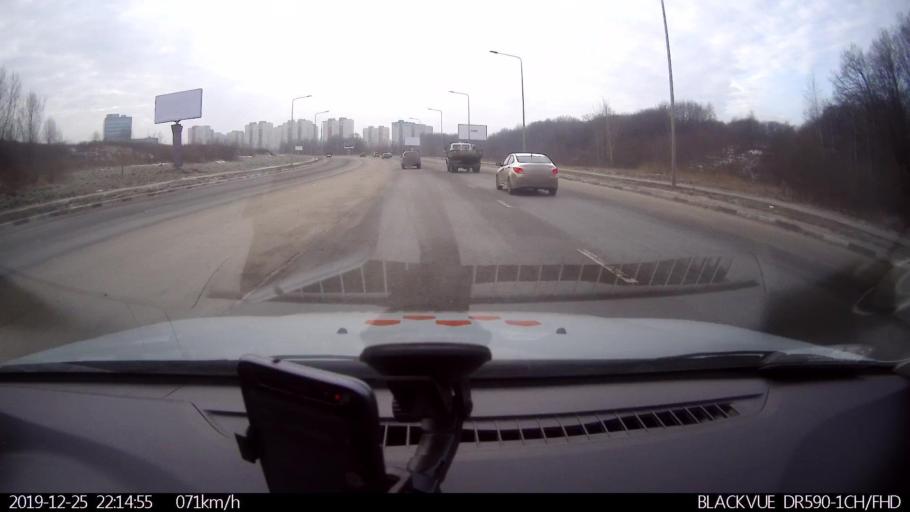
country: RU
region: Nizjnij Novgorod
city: Nizhniy Novgorod
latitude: 56.2725
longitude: 44.0261
